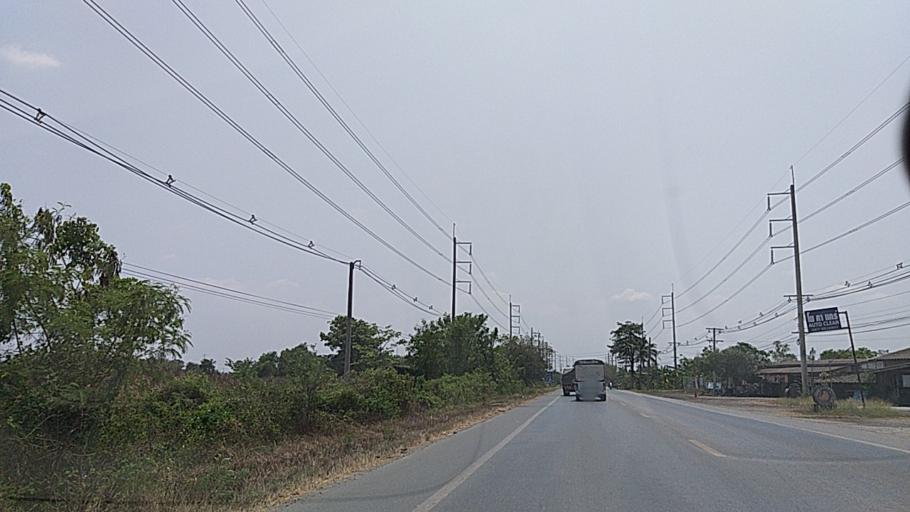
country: TH
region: Chachoengsao
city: Bang Nam Priao
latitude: 13.8371
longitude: 101.0542
